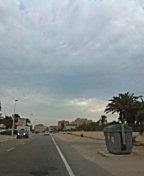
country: ES
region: Murcia
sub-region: Murcia
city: La Manga del Mar Menor
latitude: 37.7299
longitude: -0.7393
